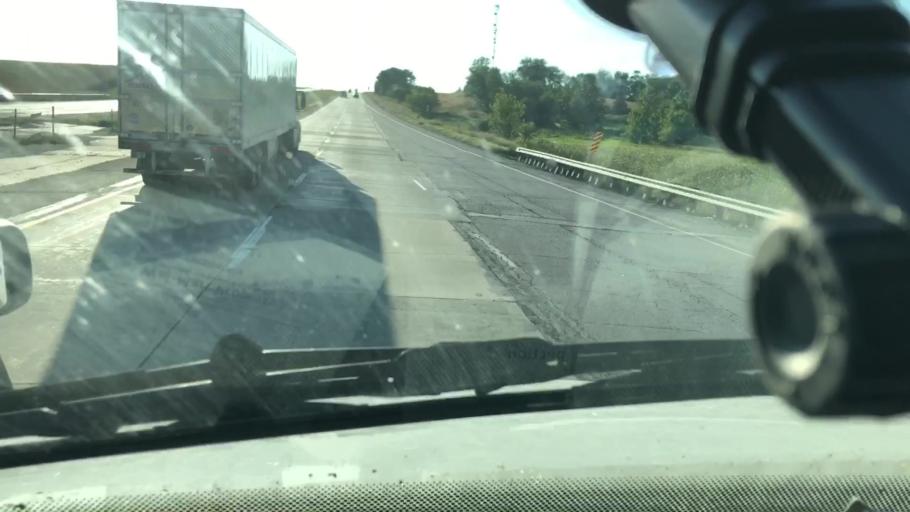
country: US
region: Iowa
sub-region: Pottawattamie County
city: Avoca
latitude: 41.4989
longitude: -95.4564
